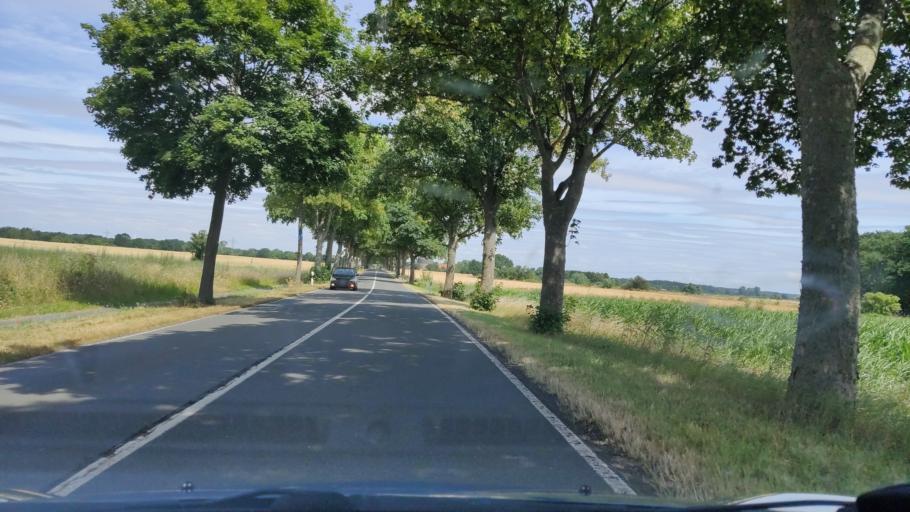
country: DE
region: Lower Saxony
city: Neustadt am Rubenberge
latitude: 52.5214
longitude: 9.4652
